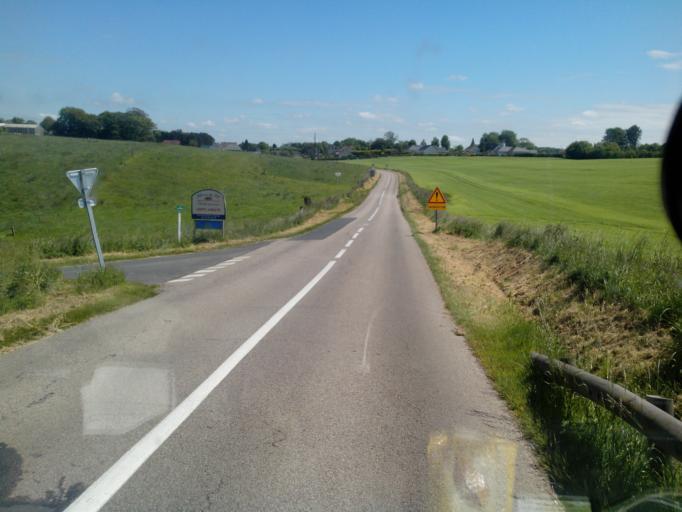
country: FR
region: Haute-Normandie
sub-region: Departement de la Seine-Maritime
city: Gonneville-la-Mallet
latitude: 49.6667
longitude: 0.1954
